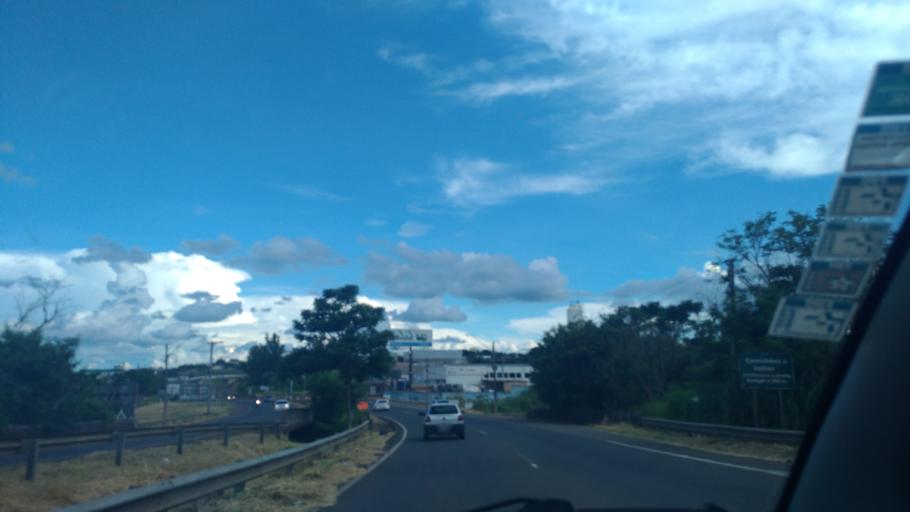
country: BR
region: Sao Paulo
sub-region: Americana
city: Americana
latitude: -22.7629
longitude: -47.3200
